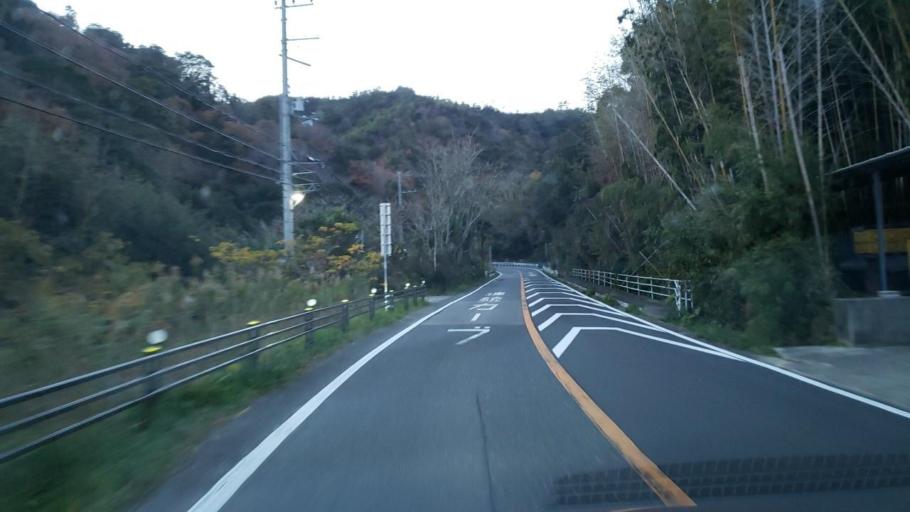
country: JP
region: Hyogo
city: Fukura
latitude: 34.2900
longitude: 134.7147
